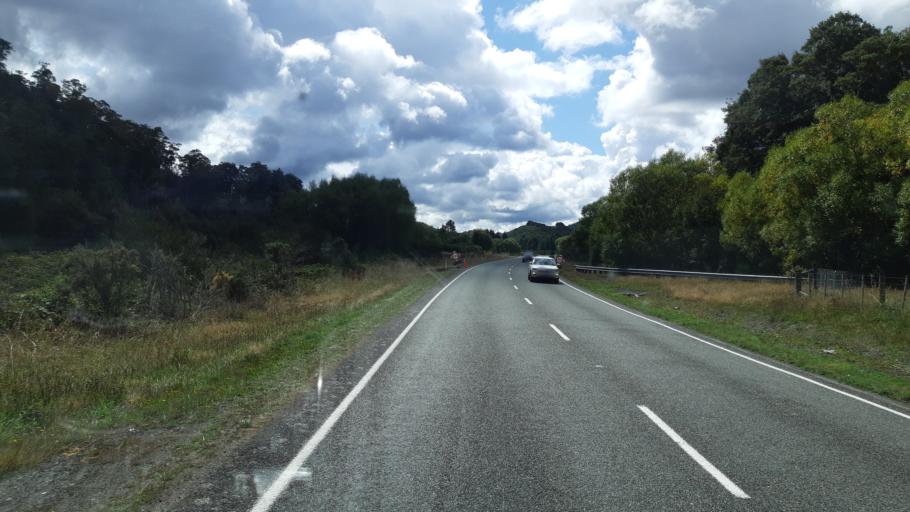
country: NZ
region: Tasman
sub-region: Tasman District
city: Wakefield
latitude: -41.6515
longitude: 172.6472
